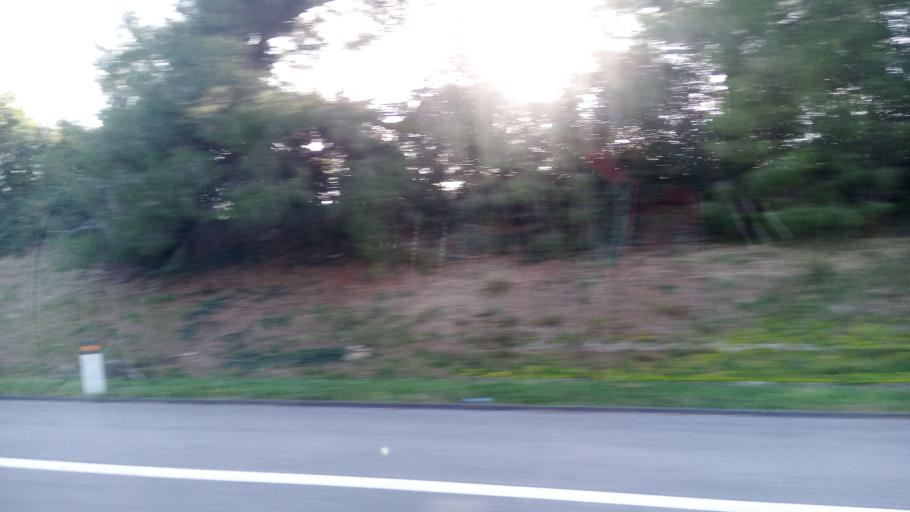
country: IT
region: Molise
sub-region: Provincia di Campobasso
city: Campomarino
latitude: 41.9463
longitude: 15.0279
